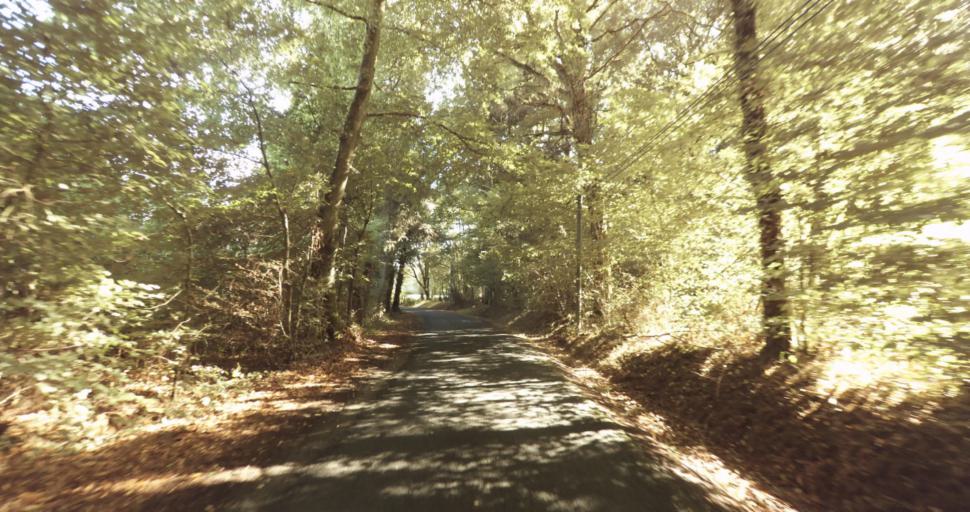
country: FR
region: Lower Normandy
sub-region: Departement de l'Orne
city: Vimoutiers
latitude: 48.9087
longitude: 0.1522
